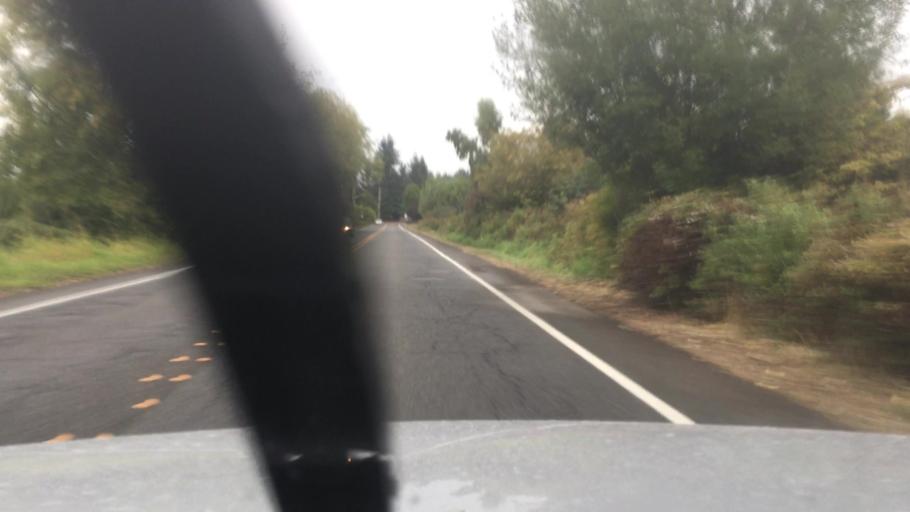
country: US
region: Washington
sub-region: King County
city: Eastgate
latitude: 47.5975
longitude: -122.1317
